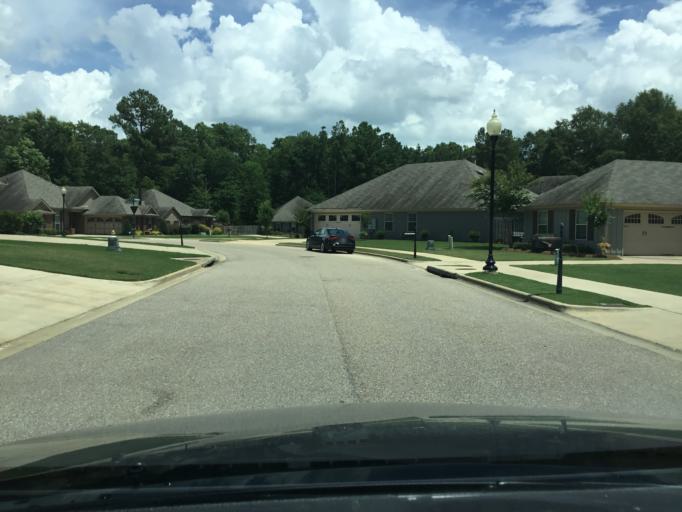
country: US
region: Alabama
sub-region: Montgomery County
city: Pike Road
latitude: 32.3384
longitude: -86.0852
